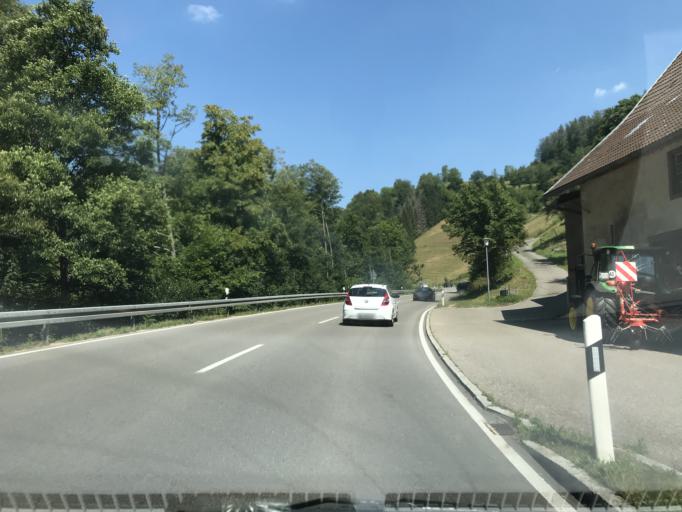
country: DE
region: Baden-Wuerttemberg
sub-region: Freiburg Region
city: Wembach
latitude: 47.7410
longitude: 7.8813
